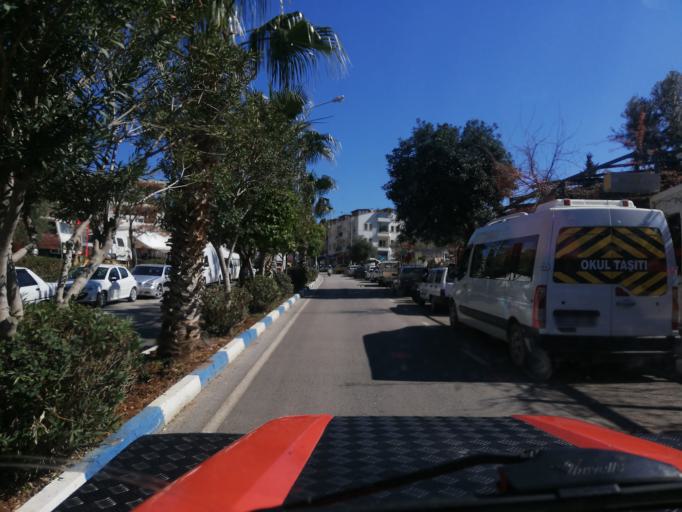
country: TR
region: Antalya
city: Kas
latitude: 36.2023
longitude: 29.6365
